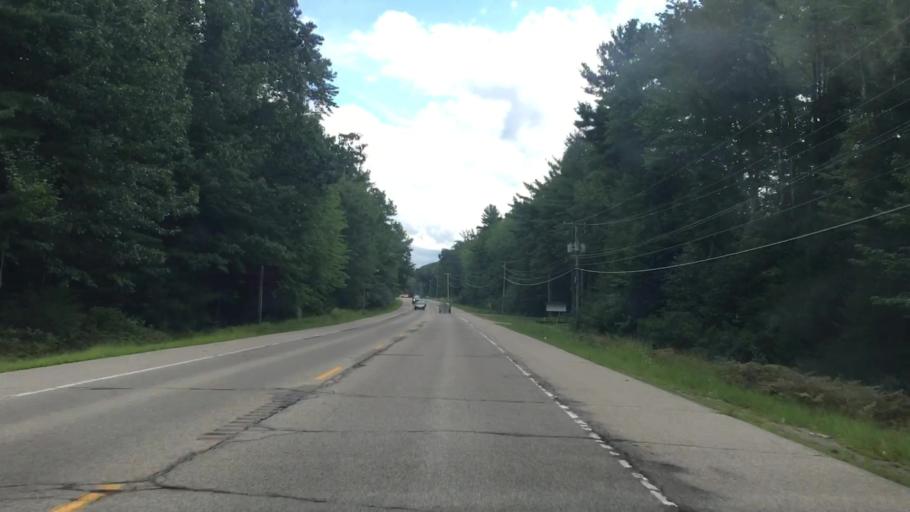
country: US
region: Maine
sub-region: York County
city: South Sanford
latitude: 43.4060
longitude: -70.7417
